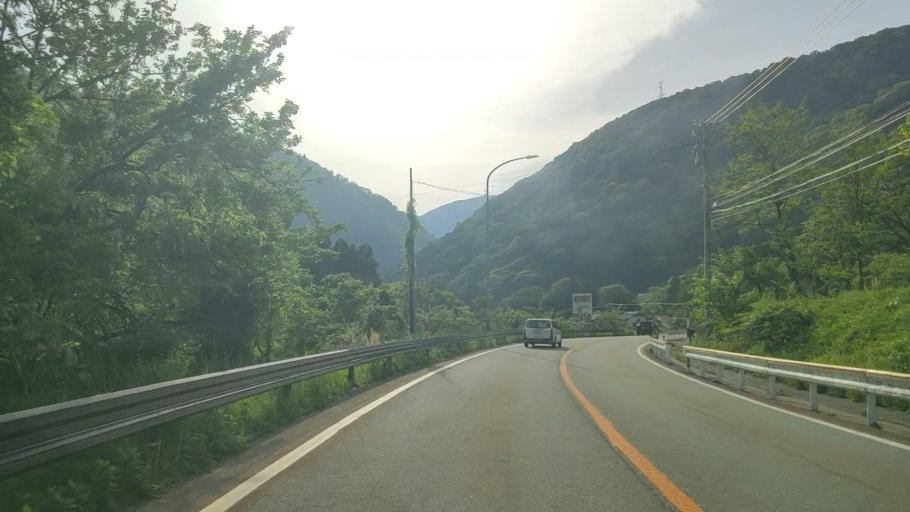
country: JP
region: Toyama
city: Yatsuomachi-higashikumisaka
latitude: 36.4495
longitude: 137.2701
